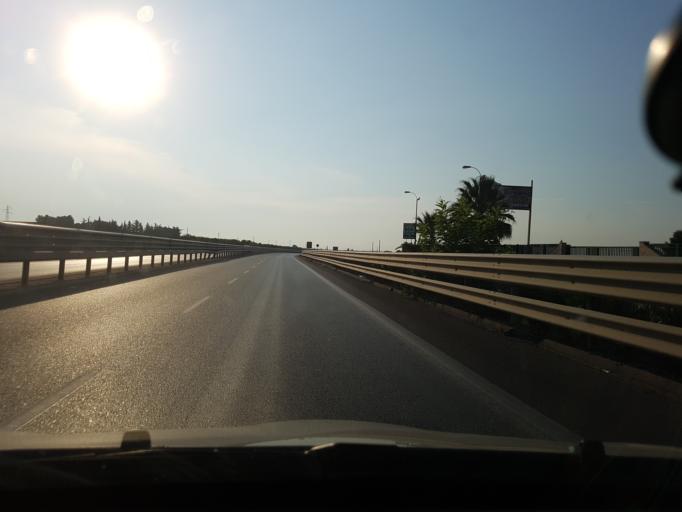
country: IT
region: Apulia
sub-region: Provincia di Foggia
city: Cerignola
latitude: 41.2812
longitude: 15.8531
